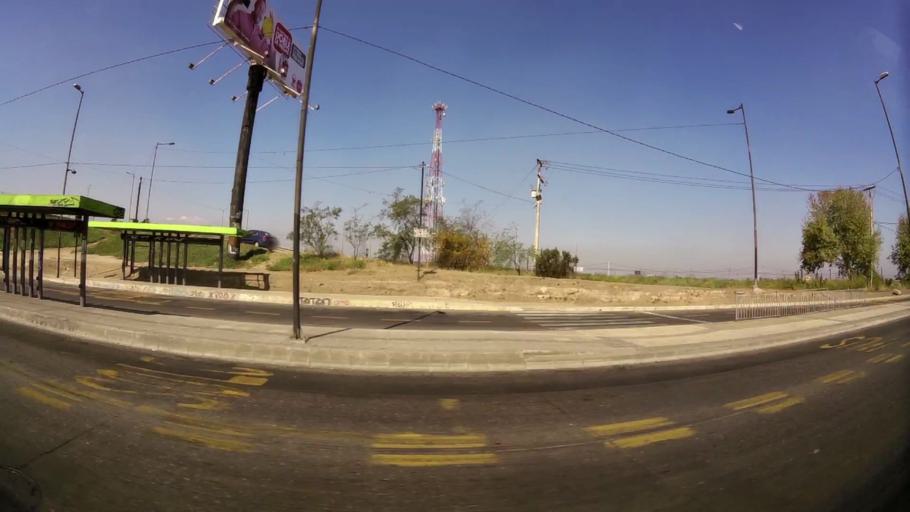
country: CL
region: Santiago Metropolitan
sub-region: Provincia de Santiago
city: Lo Prado
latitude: -33.4889
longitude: -70.7518
